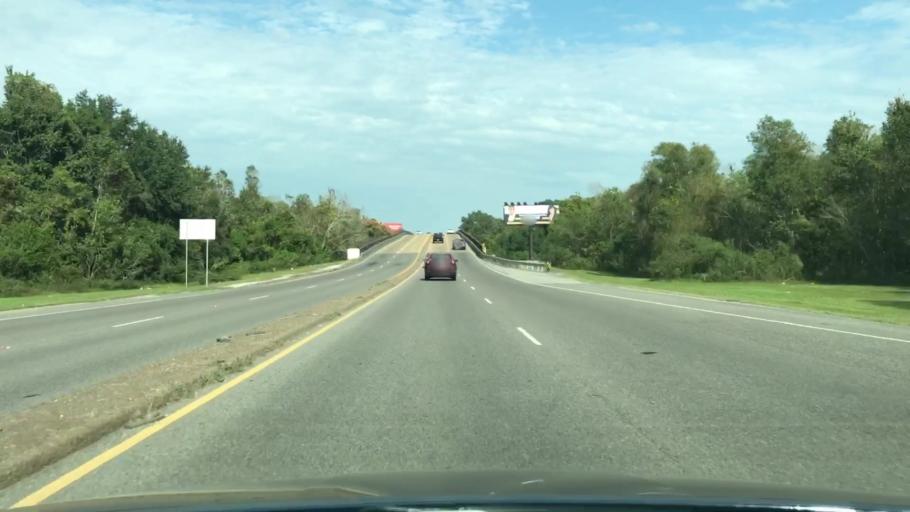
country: US
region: Louisiana
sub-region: Jefferson Parish
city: Bridge City
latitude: 29.9136
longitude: -90.1758
